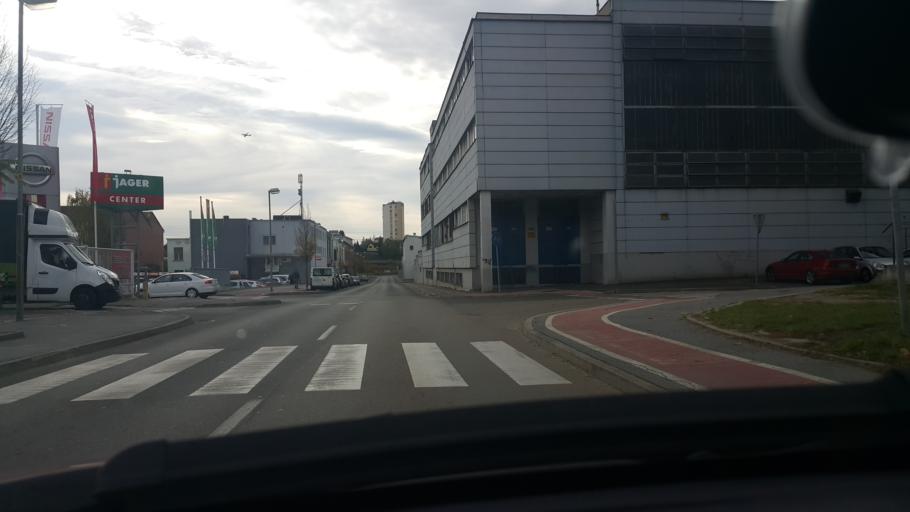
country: SI
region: Maribor
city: Maribor
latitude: 46.5589
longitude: 15.6640
